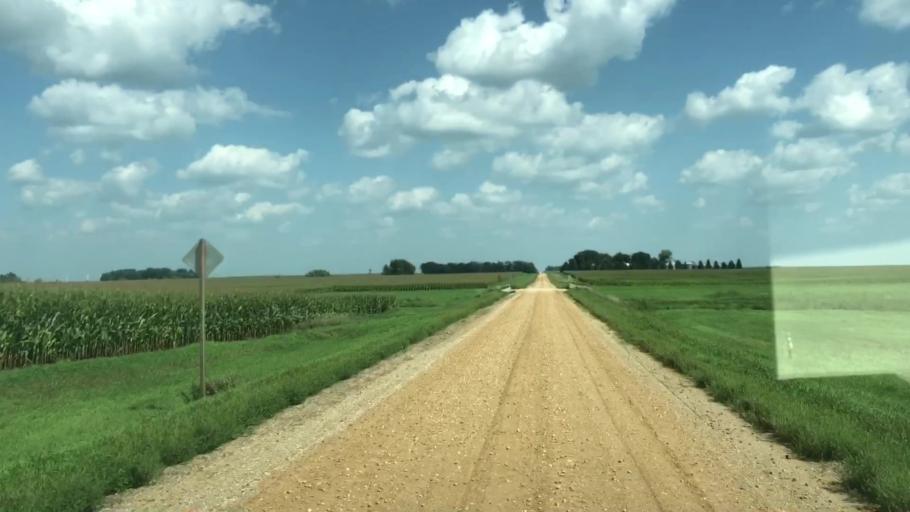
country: US
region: Iowa
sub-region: O'Brien County
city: Sheldon
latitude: 43.1568
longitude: -95.8006
